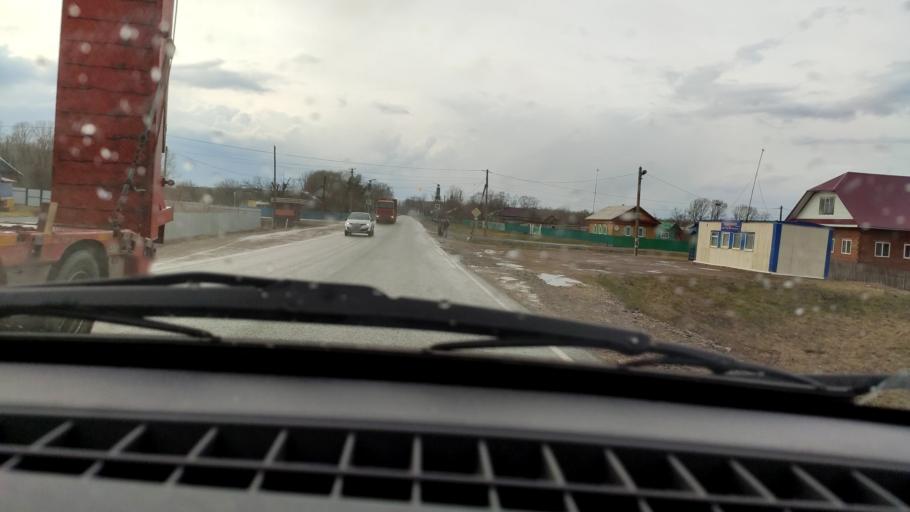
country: RU
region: Bashkortostan
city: Alekseyevka
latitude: 55.0728
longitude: 55.0849
